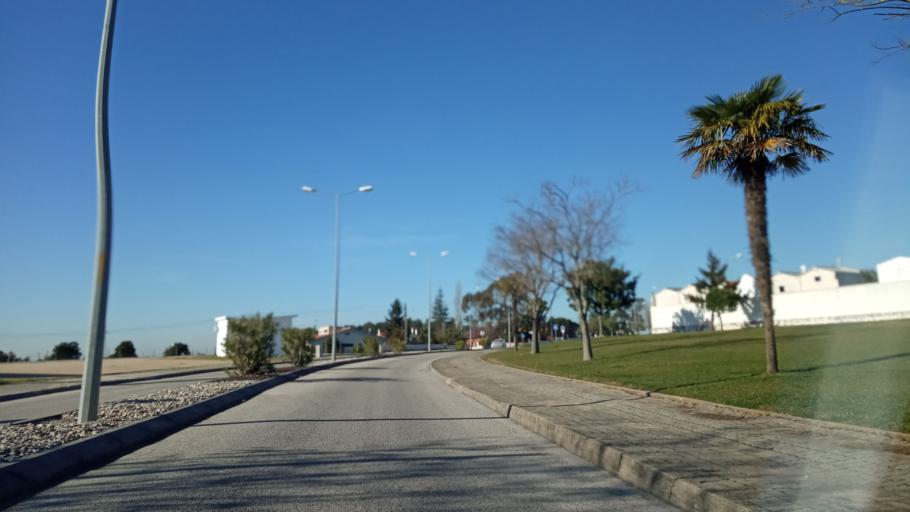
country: PT
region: Aveiro
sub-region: Anadia
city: Anadia
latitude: 40.4364
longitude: -8.4421
